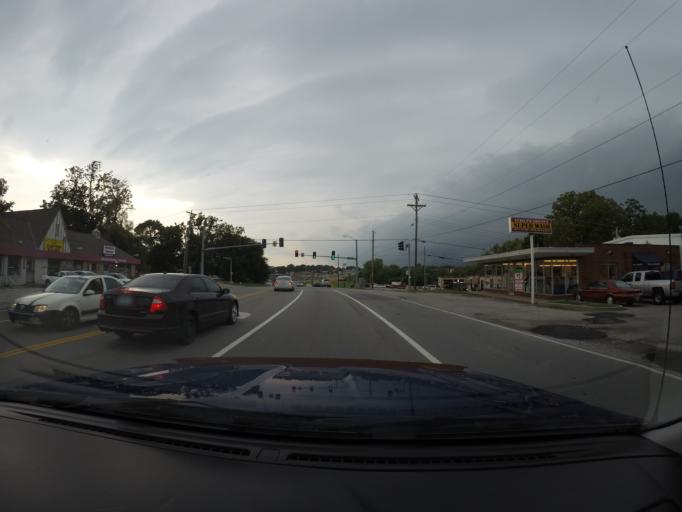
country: US
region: Missouri
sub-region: Jackson County
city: Independence
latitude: 39.1023
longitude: -94.4028
